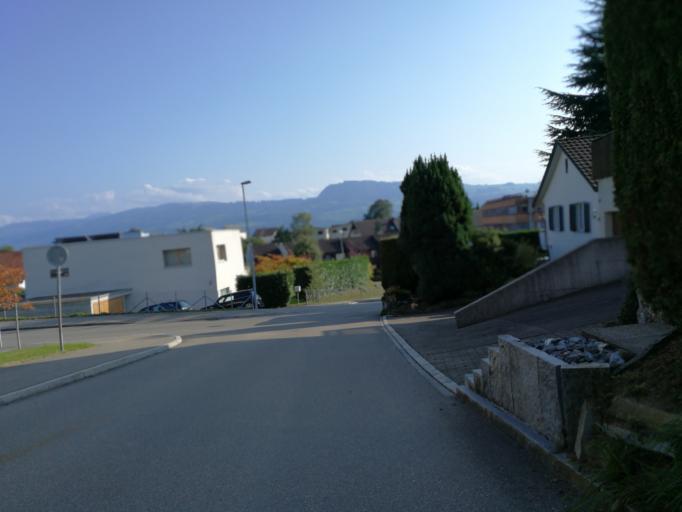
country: CH
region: Zurich
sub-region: Bezirk Meilen
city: Uerikon
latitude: 47.2394
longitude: 8.7500
